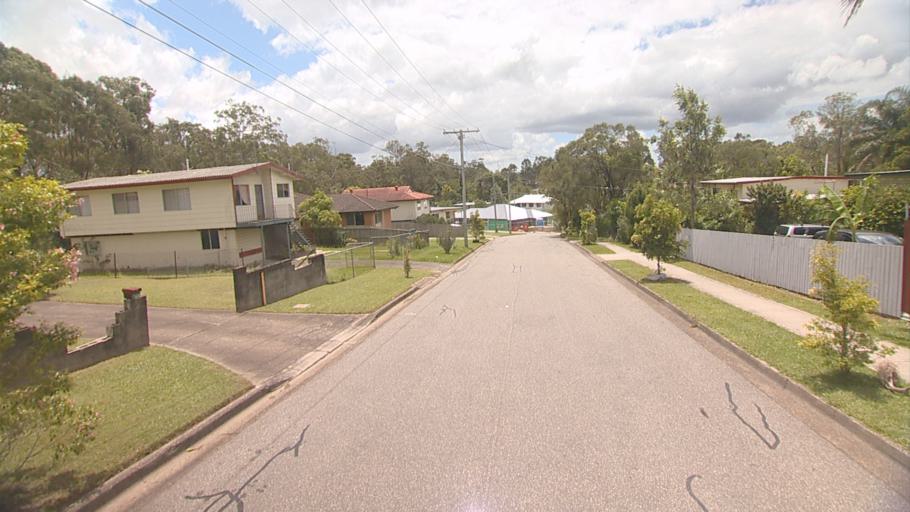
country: AU
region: Queensland
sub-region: Logan
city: Woodridge
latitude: -27.6255
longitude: 153.0974
